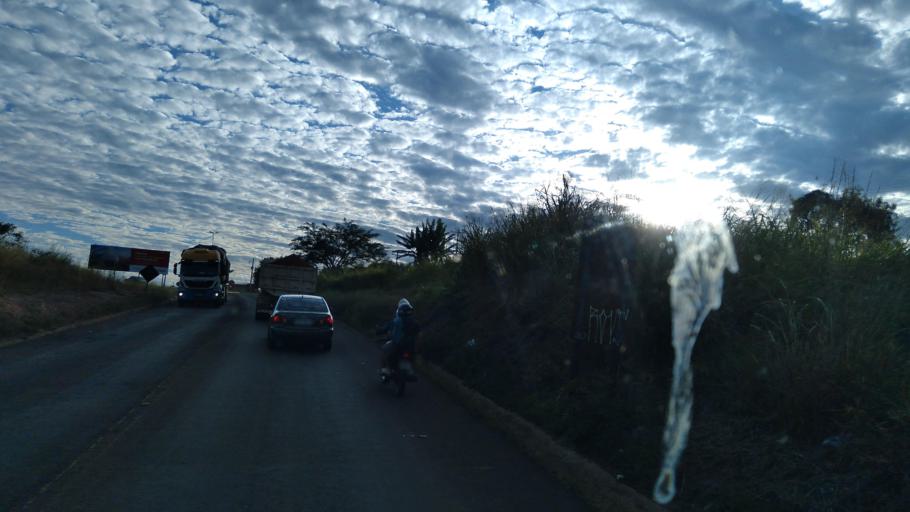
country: BR
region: Goias
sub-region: Mineiros
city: Mineiros
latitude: -17.5781
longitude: -52.5346
